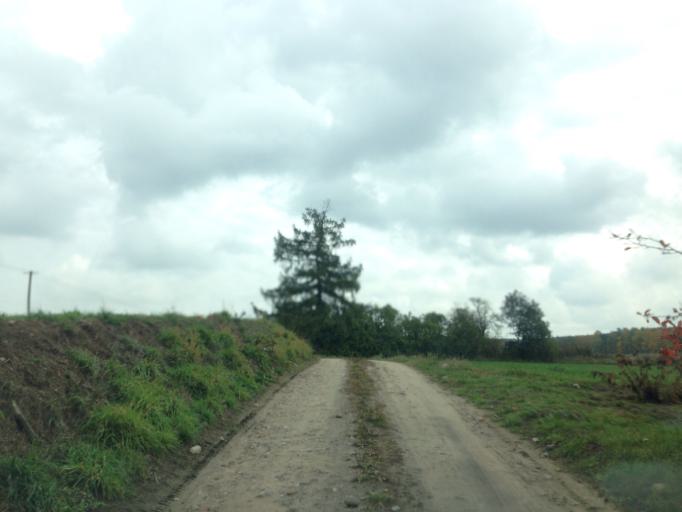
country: PL
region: Kujawsko-Pomorskie
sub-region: Powiat brodnicki
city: Gorzno
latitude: 53.2549
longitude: 19.6792
